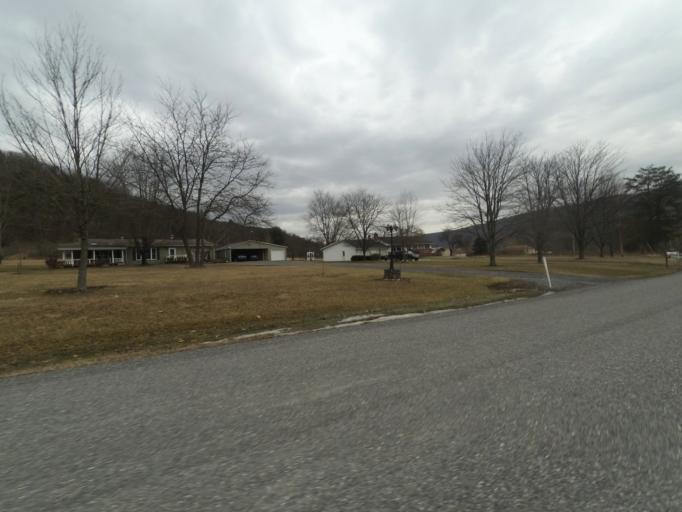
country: US
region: Pennsylvania
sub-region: Centre County
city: Park Forest Village
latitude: 40.8510
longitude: -77.9733
